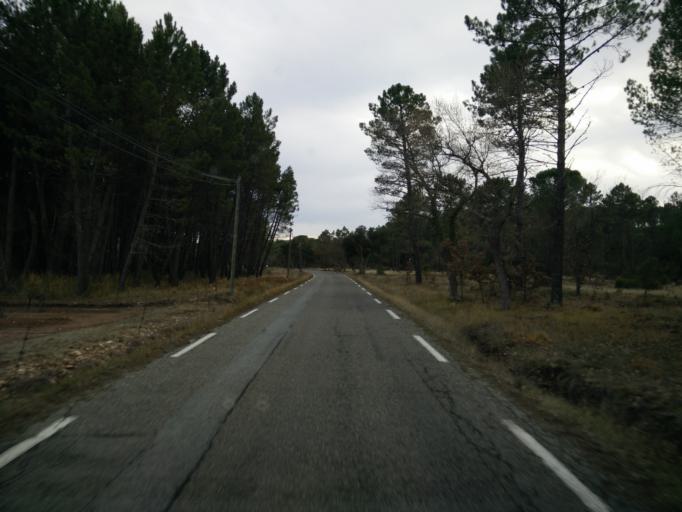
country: FR
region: Provence-Alpes-Cote d'Azur
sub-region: Departement du Var
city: Vidauban
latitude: 43.3773
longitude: 6.4425
